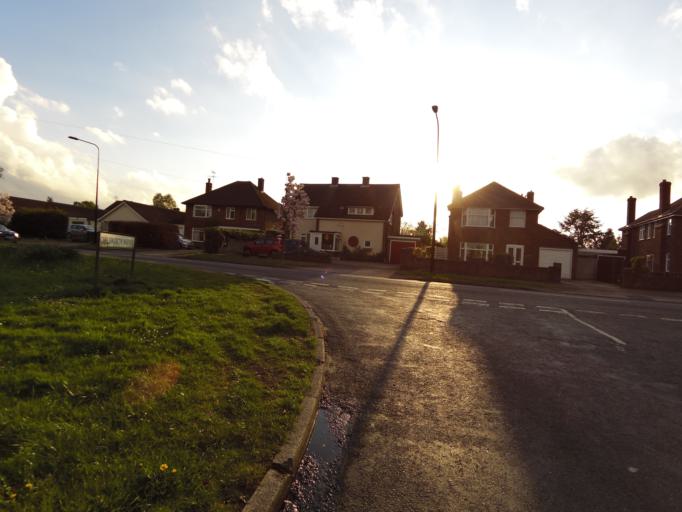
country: GB
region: England
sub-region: Suffolk
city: Ipswich
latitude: 52.0723
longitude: 1.1629
